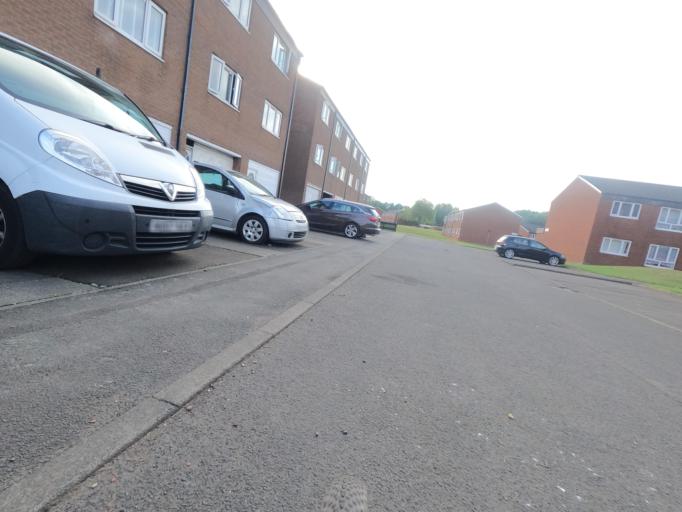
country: GB
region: England
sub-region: Northumberland
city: Cramlington
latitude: 55.0866
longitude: -1.6095
